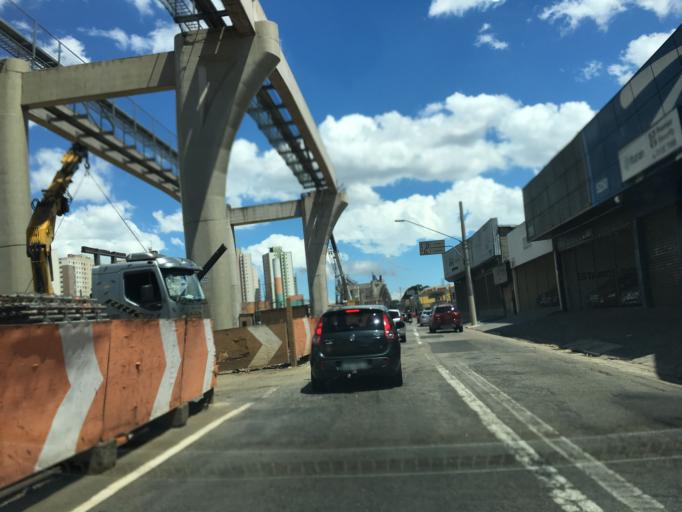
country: BR
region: Sao Paulo
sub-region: Sao Caetano Do Sul
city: Sao Caetano do Sul
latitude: -23.5881
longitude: -46.5454
